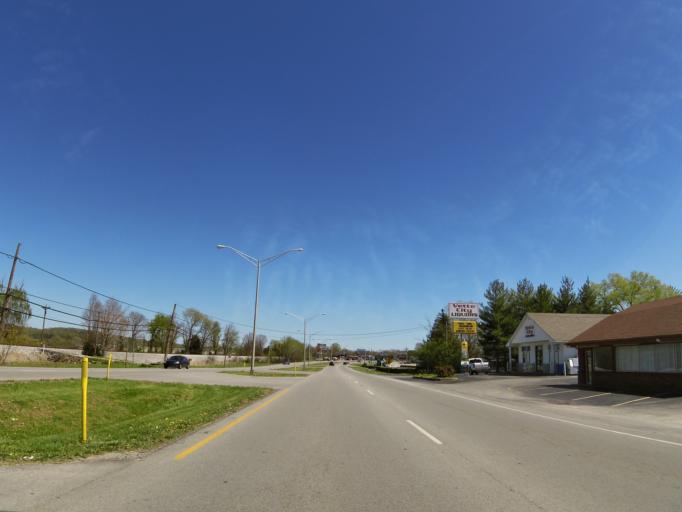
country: US
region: Kentucky
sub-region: Warren County
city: Bowling Green
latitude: 37.0101
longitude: -86.3985
